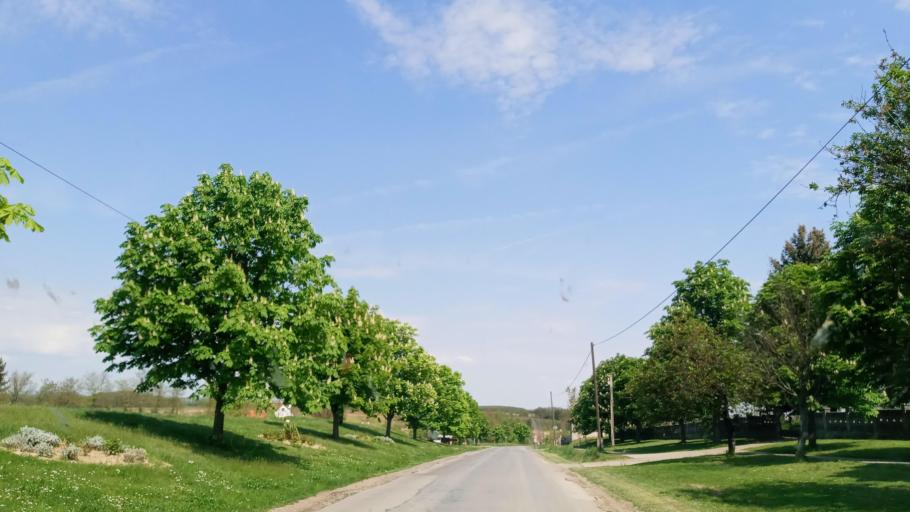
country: HU
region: Baranya
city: Boly
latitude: 45.9187
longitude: 18.5442
